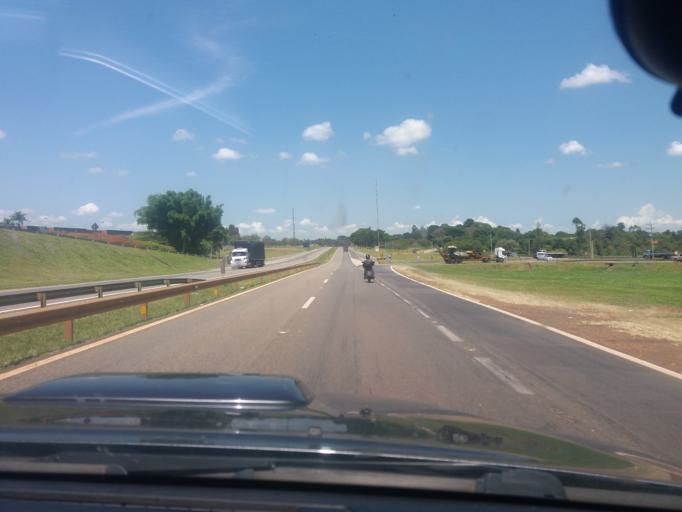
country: BR
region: Sao Paulo
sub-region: Tatui
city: Tatui
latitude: -23.3597
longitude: -47.8877
